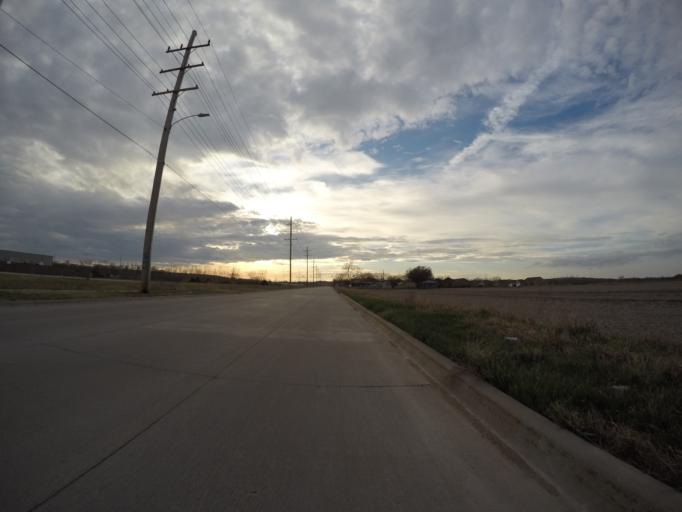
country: US
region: Kansas
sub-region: Riley County
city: Manhattan
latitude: 39.2187
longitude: -96.5700
